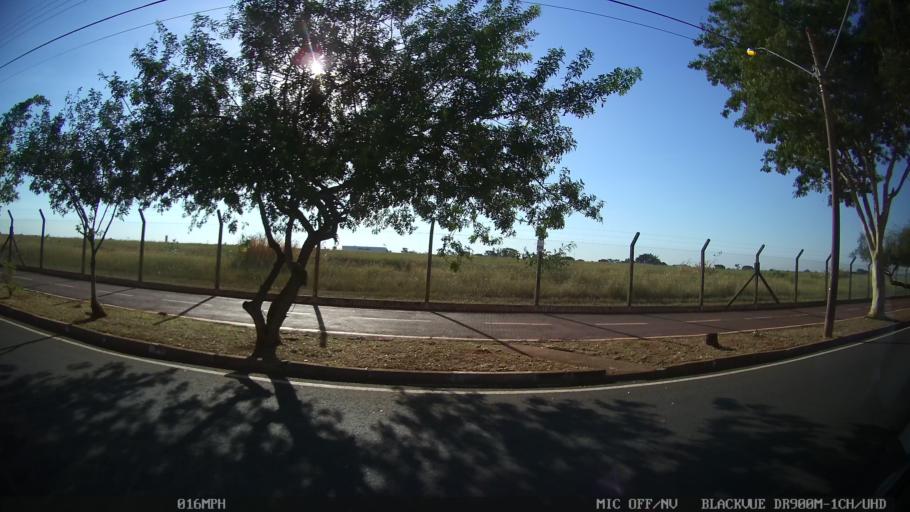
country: BR
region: Sao Paulo
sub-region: Sao Jose Do Rio Preto
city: Sao Jose do Rio Preto
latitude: -20.8207
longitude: -49.4098
